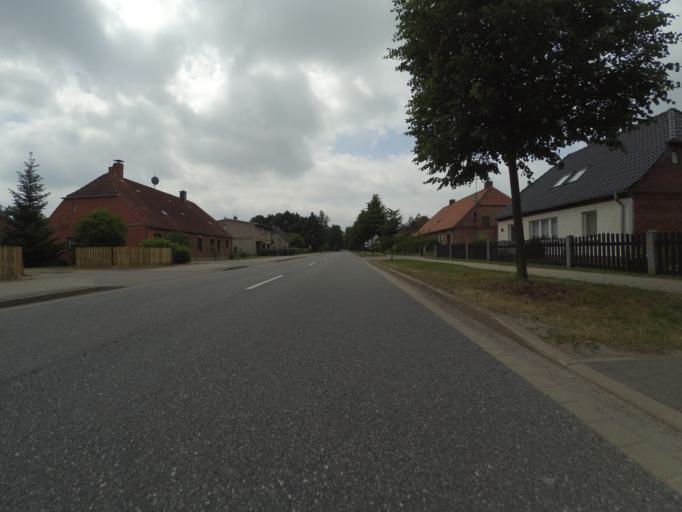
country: DE
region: Mecklenburg-Vorpommern
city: Malchow
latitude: 53.5311
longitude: 12.4238
